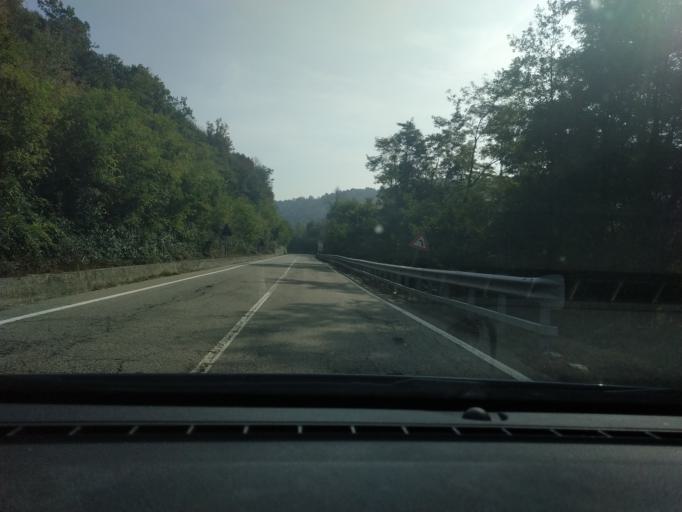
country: IT
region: Piedmont
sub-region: Provincia di Biella
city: Sala Biellese
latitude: 45.5202
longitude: 7.9546
